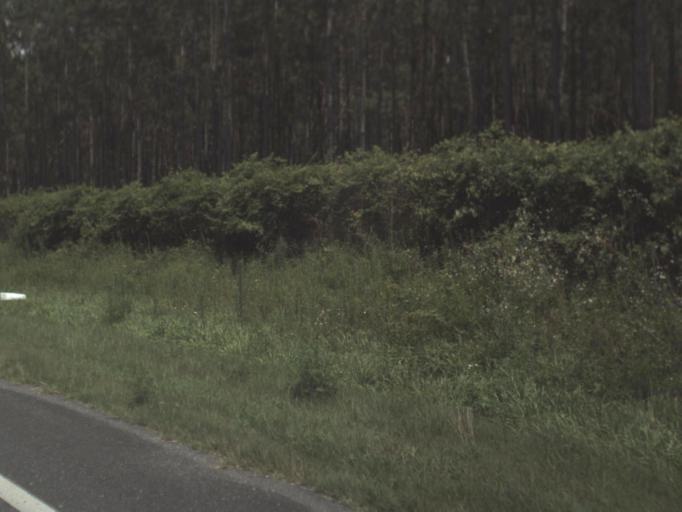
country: US
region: Florida
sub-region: Gilchrist County
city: Trenton
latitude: 29.6159
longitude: -82.7926
